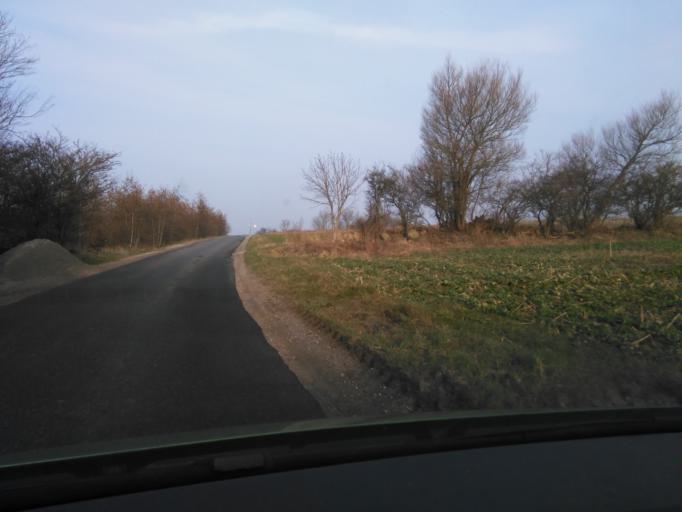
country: DK
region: Central Jutland
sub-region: Arhus Kommune
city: Marslet
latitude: 56.0872
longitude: 10.1625
